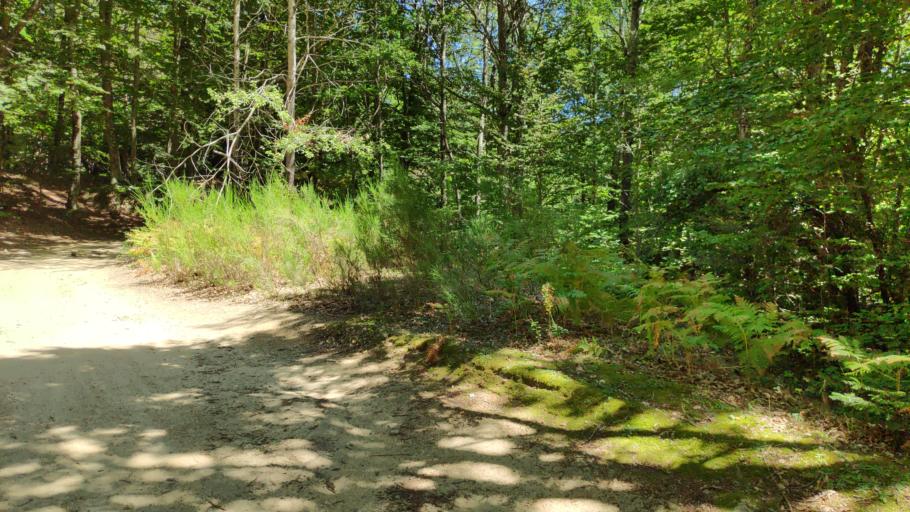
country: IT
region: Calabria
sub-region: Provincia di Vibo-Valentia
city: Mongiana
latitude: 38.5332
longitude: 16.3746
